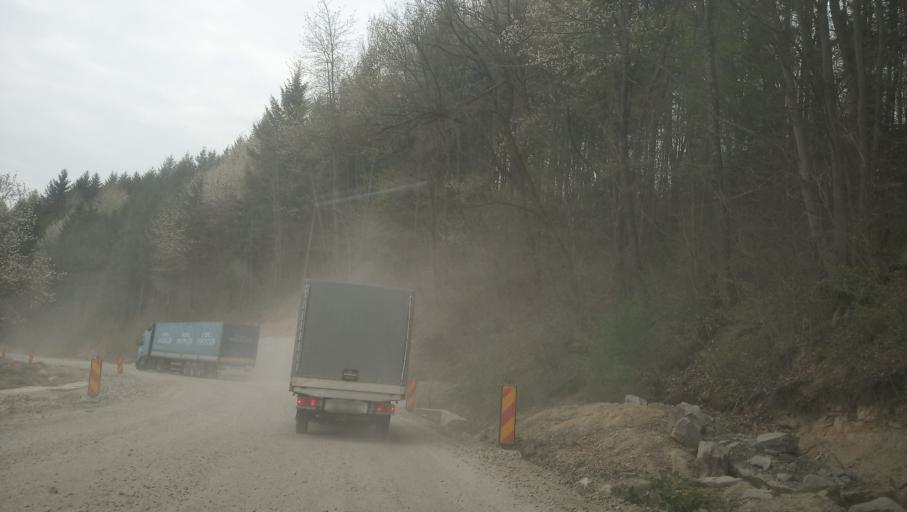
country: RO
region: Bihor
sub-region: Comuna Cristioru de Jos
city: Cristioru de Jos
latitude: 46.3725
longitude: 22.5534
